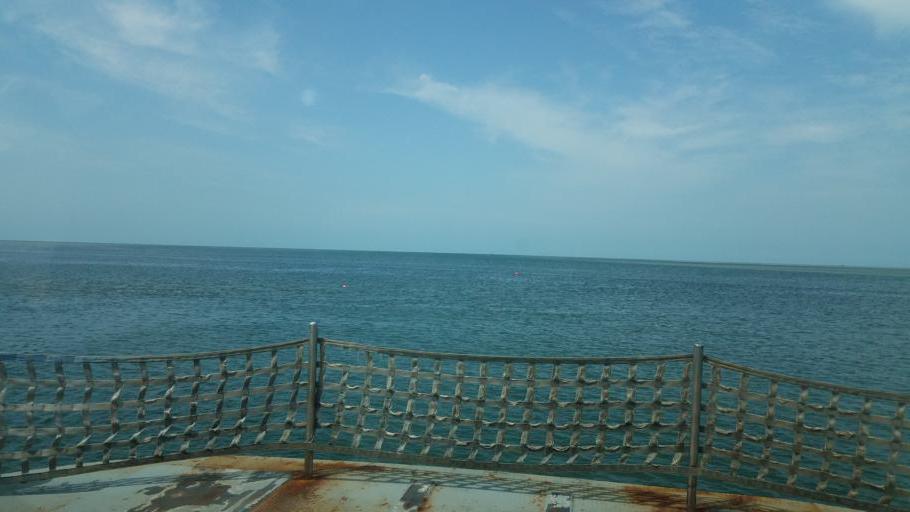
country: US
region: North Carolina
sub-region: Dare County
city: Buxton
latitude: 35.1945
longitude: -75.7817
